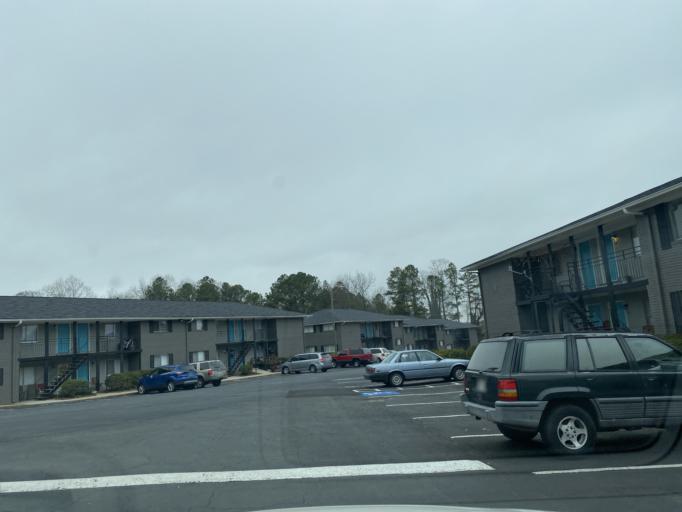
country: US
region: Georgia
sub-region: Cobb County
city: Fair Oaks
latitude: 33.9051
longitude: -84.5671
